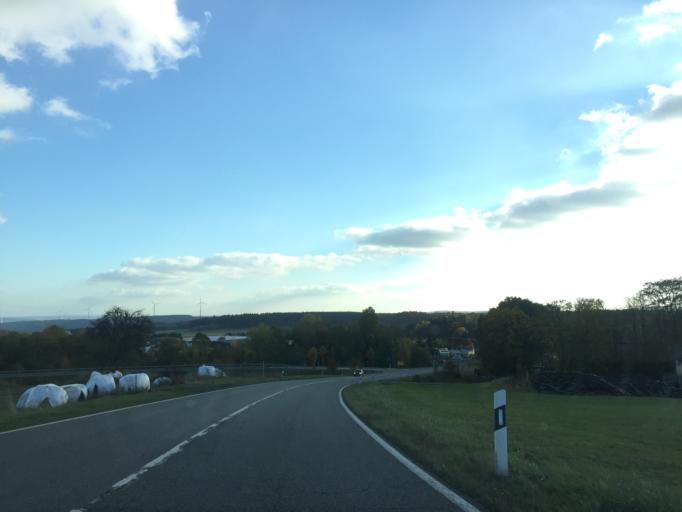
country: DE
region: Rheinland-Pfalz
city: Weroth
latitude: 50.4524
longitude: 7.9442
